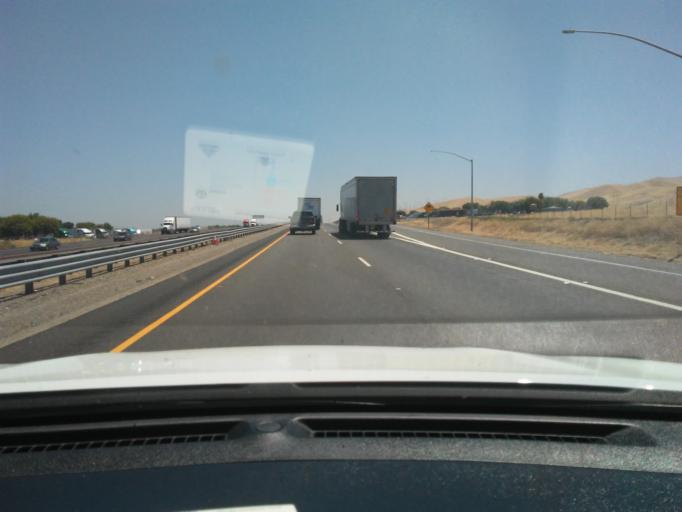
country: US
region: California
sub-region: San Joaquin County
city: Tracy
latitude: 37.5845
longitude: -121.3255
